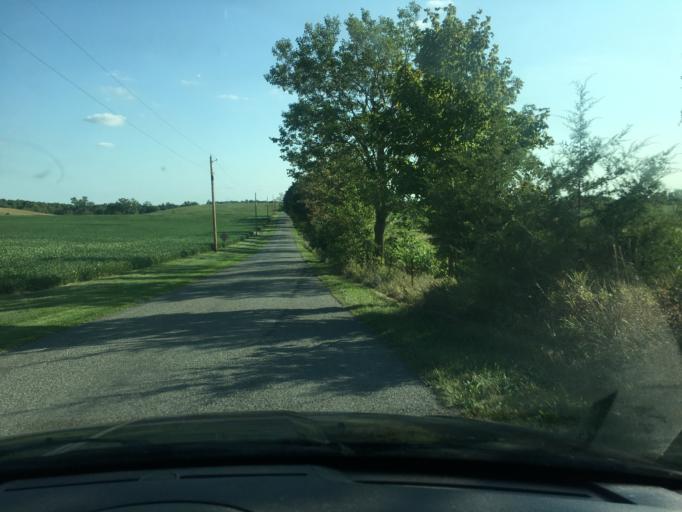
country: US
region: Ohio
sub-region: Logan County
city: West Liberty
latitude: 40.2866
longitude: -83.8006
